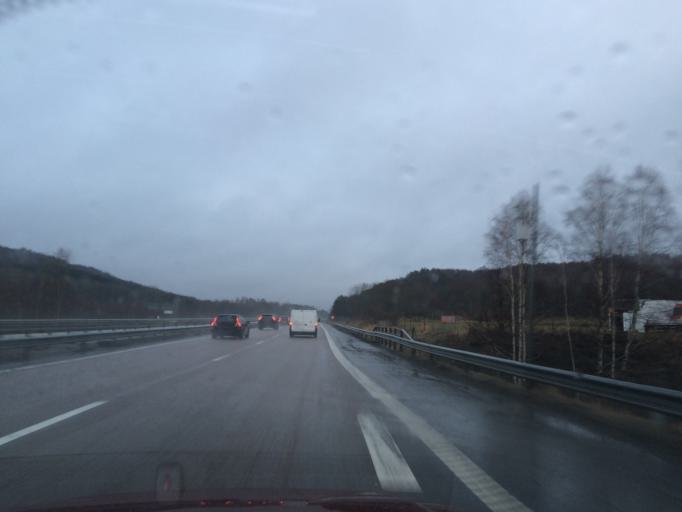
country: SE
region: Halland
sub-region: Kungsbacka Kommun
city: Kungsbacka
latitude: 57.5163
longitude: 12.0511
